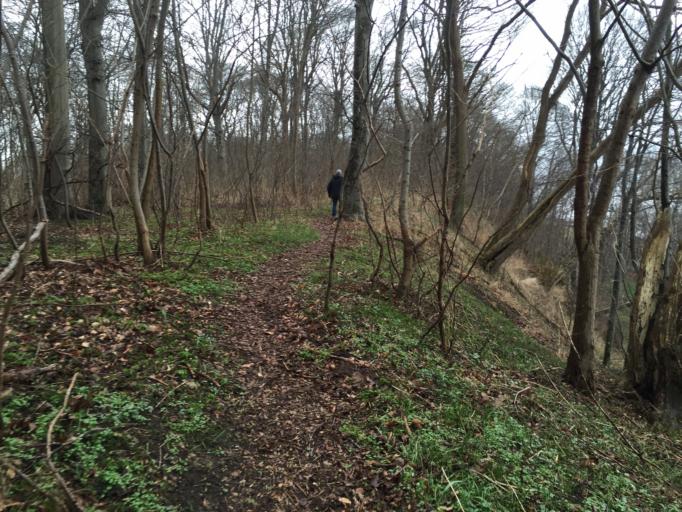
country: DK
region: South Denmark
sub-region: Assens Kommune
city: Harby
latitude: 55.1459
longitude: 10.0280
